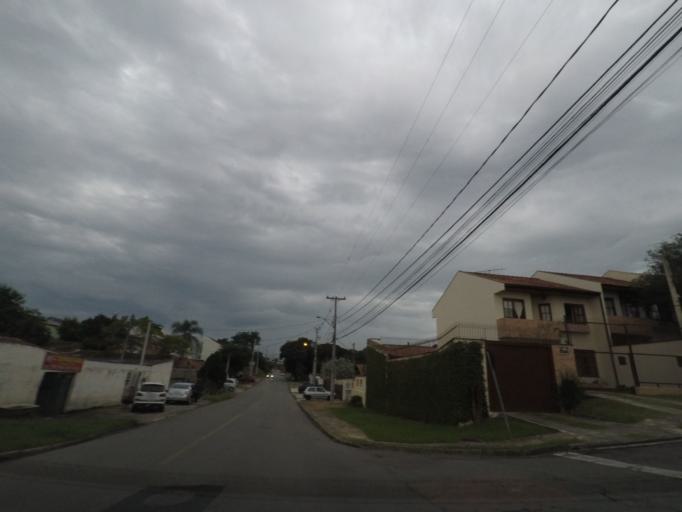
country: BR
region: Parana
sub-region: Curitiba
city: Curitiba
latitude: -25.4674
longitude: -49.3127
